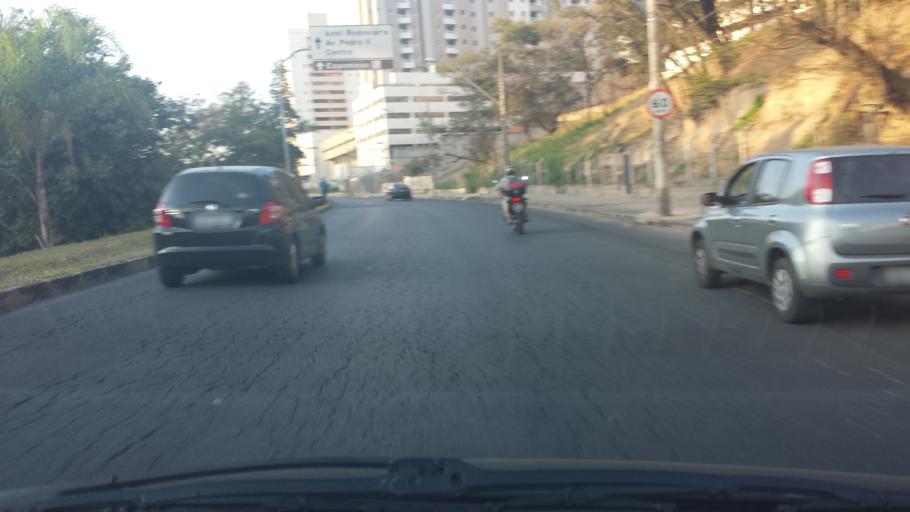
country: BR
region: Minas Gerais
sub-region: Belo Horizonte
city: Belo Horizonte
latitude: -19.8865
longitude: -43.9941
